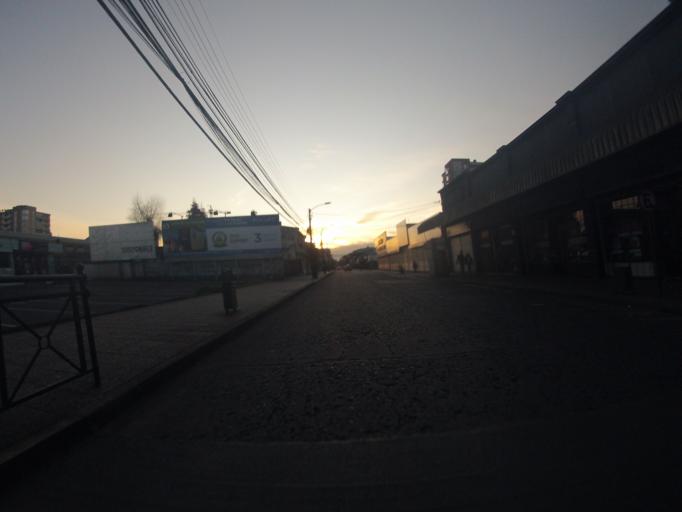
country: CL
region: Araucania
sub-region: Provincia de Cautin
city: Temuco
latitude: -38.7380
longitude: -72.5933
